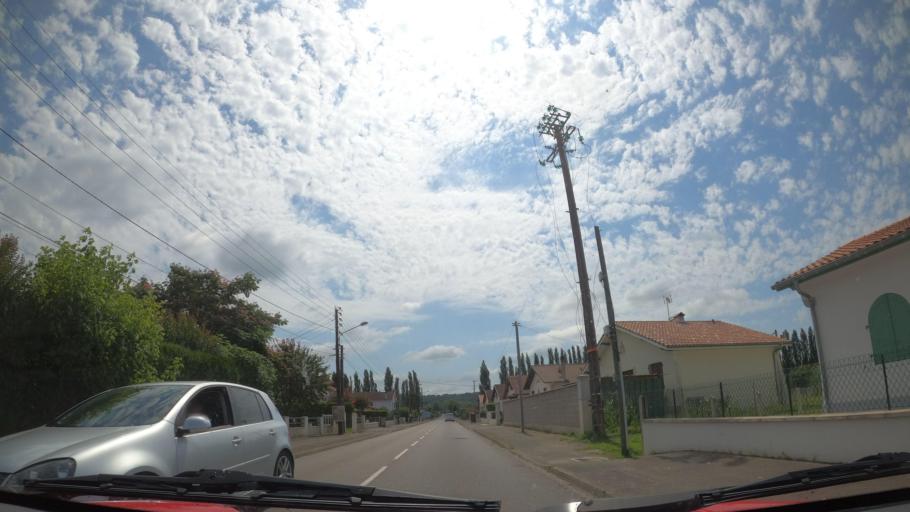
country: FR
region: Aquitaine
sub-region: Departement des Landes
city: Peyrehorade
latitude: 43.5401
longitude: -1.1069
